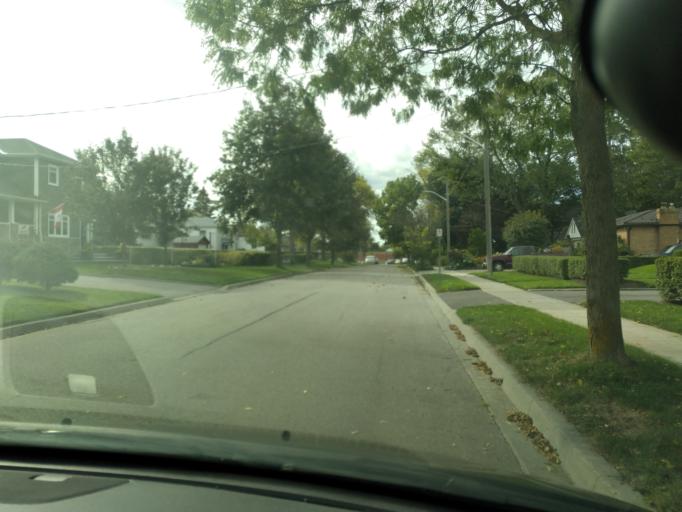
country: CA
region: Ontario
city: Newmarket
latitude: 44.0564
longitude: -79.4449
